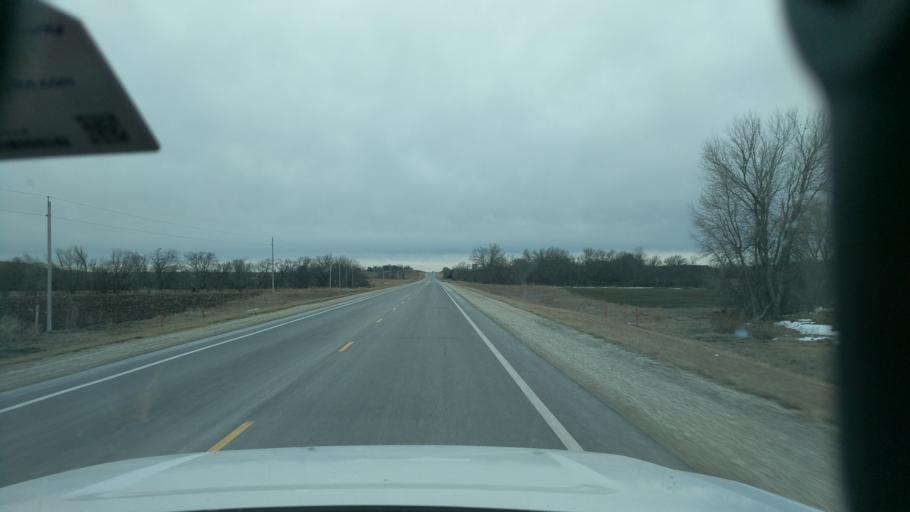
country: US
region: Kansas
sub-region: Marion County
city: Marion
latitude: 38.4442
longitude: -96.9577
